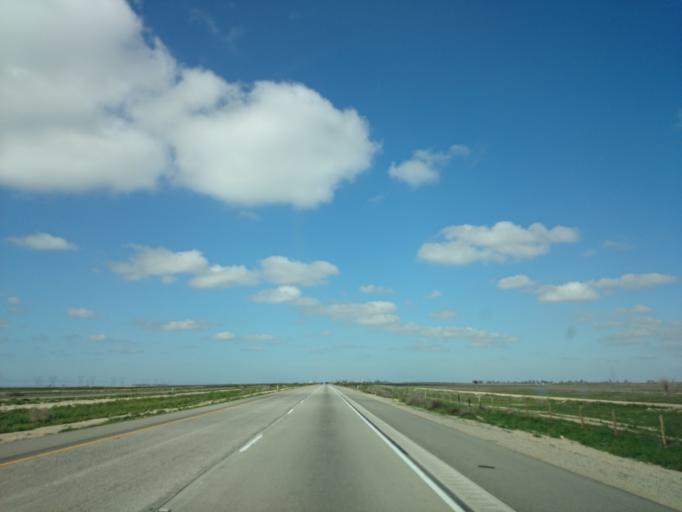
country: US
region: California
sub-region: Kern County
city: Rosedale
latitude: 35.3334
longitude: -119.3054
